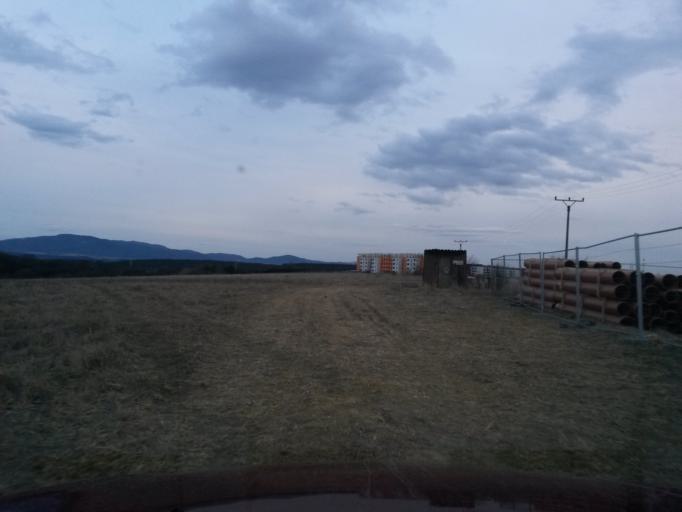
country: SK
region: Kosicky
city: Kosice
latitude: 48.7261
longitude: 21.2946
